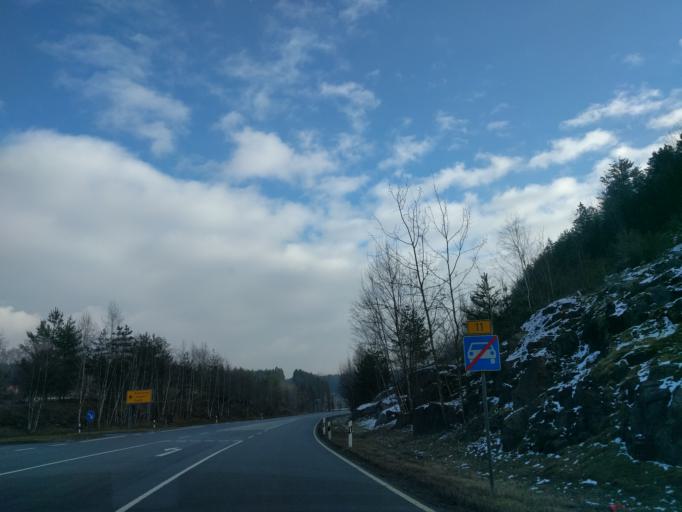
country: DE
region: Bavaria
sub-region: Lower Bavaria
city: Regen
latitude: 48.9754
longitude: 13.1478
